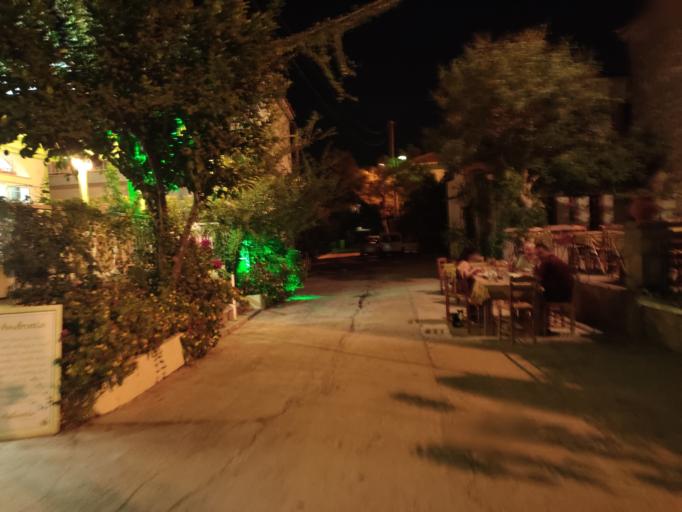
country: GR
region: North Aegean
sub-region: Nomos Lesvou
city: Kalloni
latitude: 39.2061
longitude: 26.2110
